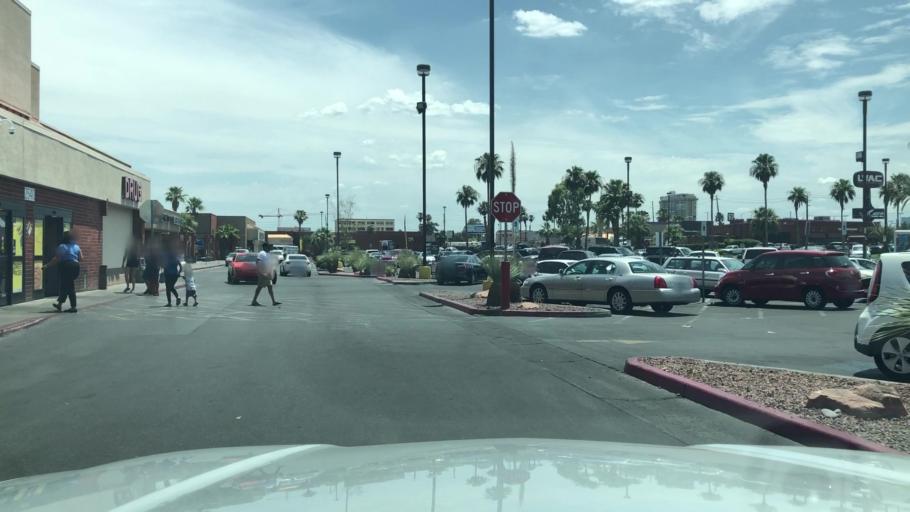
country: US
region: Nevada
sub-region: Clark County
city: Winchester
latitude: 36.1436
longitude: -115.1354
